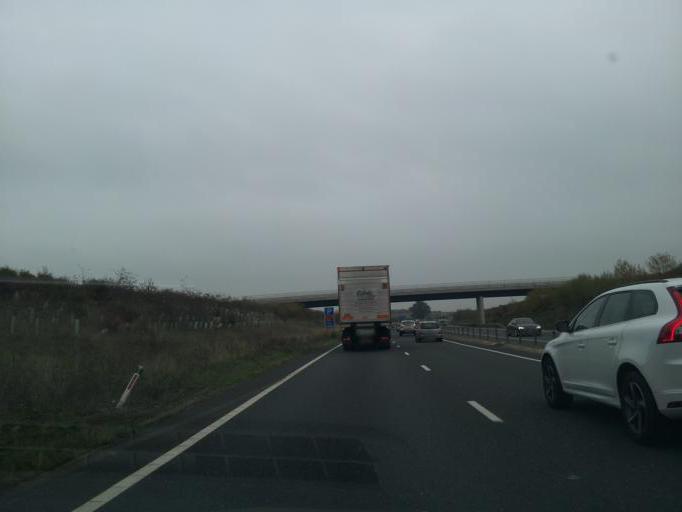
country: GB
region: England
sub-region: Bedford
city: Great Barford
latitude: 52.1666
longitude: -0.3641
